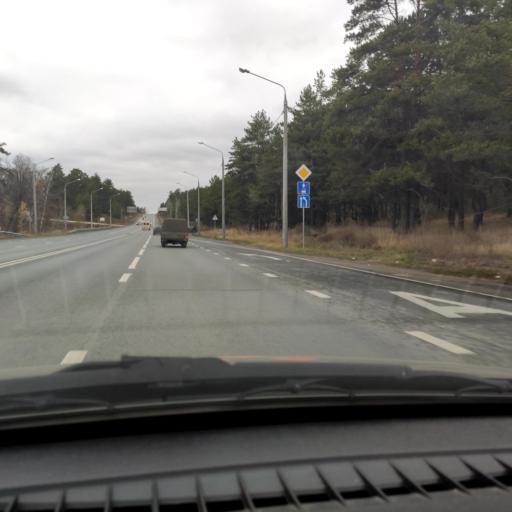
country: RU
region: Samara
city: Volzhskiy
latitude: 53.4388
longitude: 50.1094
